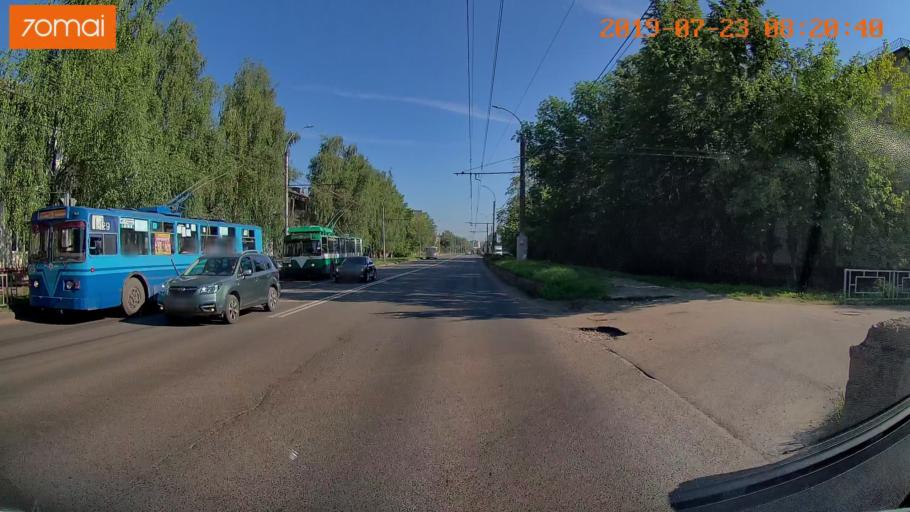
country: RU
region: Ivanovo
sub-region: Gorod Ivanovo
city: Ivanovo
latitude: 56.9698
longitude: 40.9636
